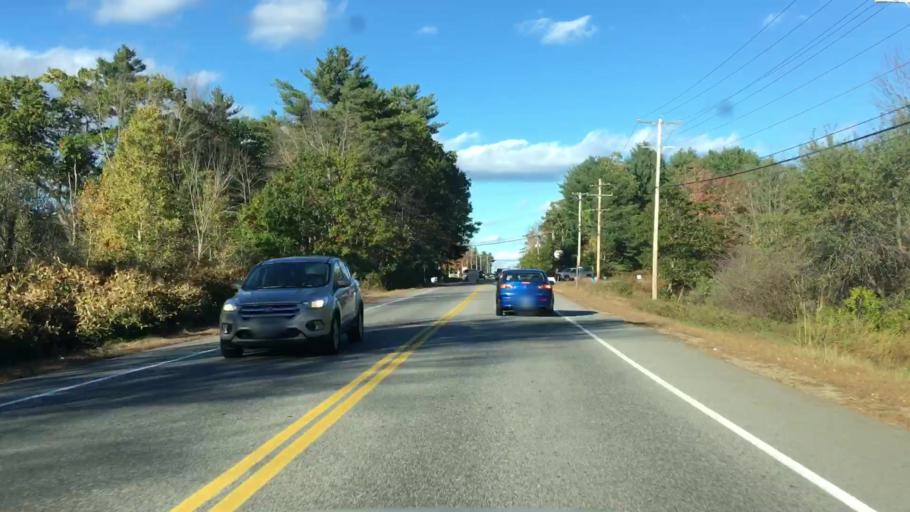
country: US
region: Maine
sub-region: Cumberland County
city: South Portland Gardens
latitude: 43.6166
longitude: -70.3548
